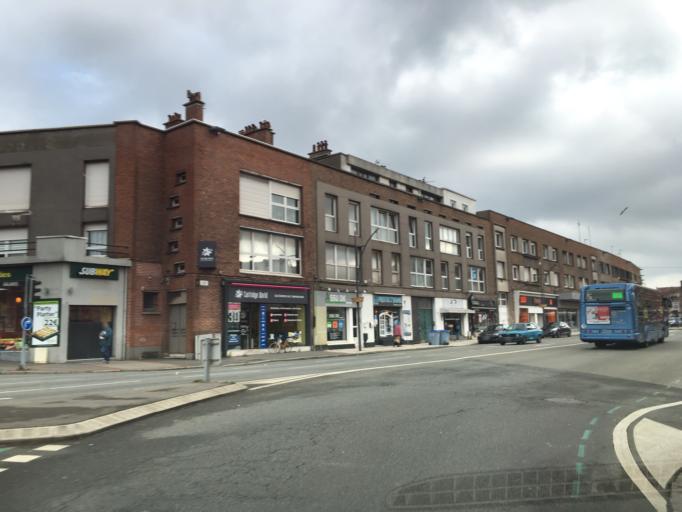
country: FR
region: Nord-Pas-de-Calais
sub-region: Departement du Nord
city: Dunkerque
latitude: 51.0319
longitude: 2.3721
